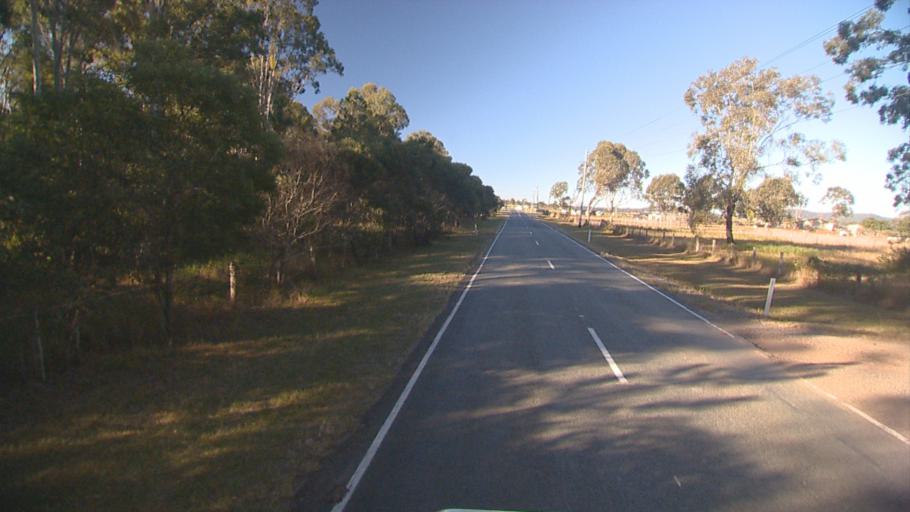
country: AU
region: Queensland
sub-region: Logan
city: Chambers Flat
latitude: -27.7542
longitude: 153.0894
